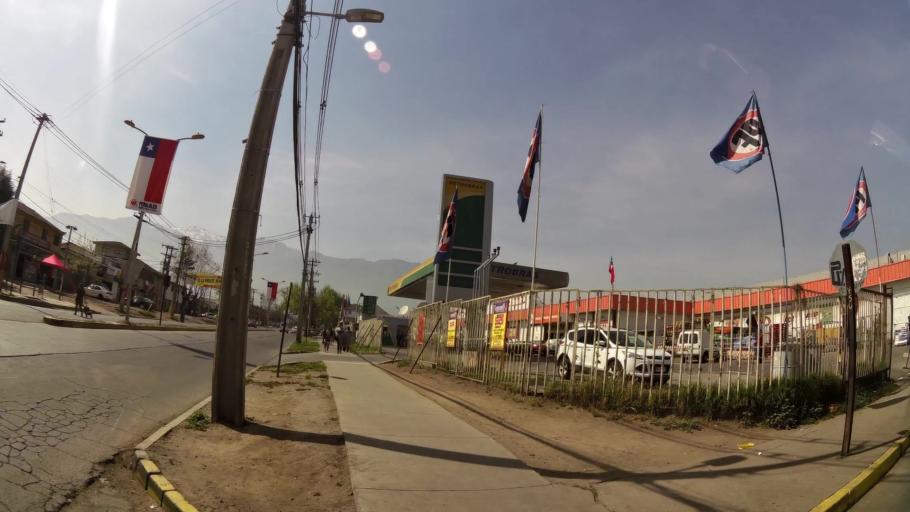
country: CL
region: Santiago Metropolitan
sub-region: Provincia de Santiago
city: Villa Presidente Frei, Nunoa, Santiago, Chile
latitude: -33.5062
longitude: -70.5801
